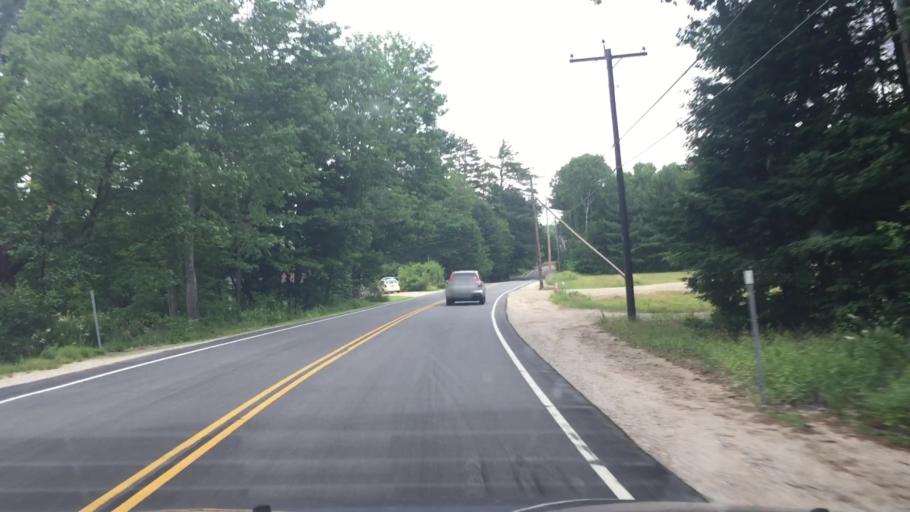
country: US
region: New Hampshire
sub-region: Carroll County
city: Tamworth
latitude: 43.8802
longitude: -71.2287
